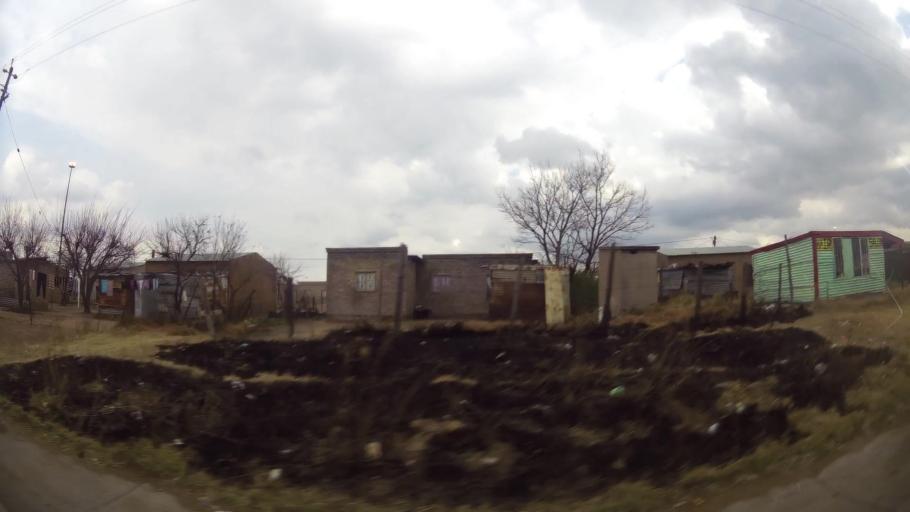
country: ZA
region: Orange Free State
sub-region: Fezile Dabi District Municipality
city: Sasolburg
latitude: -26.8551
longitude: 27.8780
